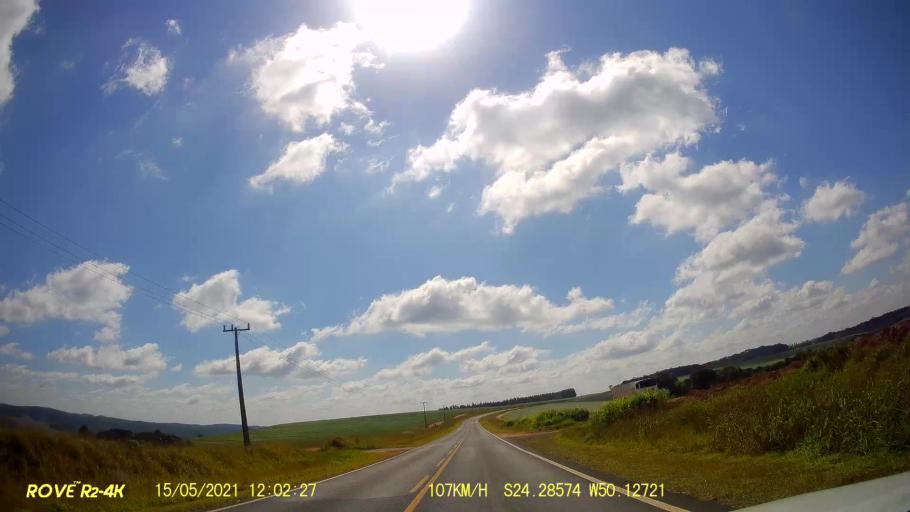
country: BR
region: Parana
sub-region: Pirai Do Sul
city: Pirai do Sul
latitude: -24.2860
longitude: -50.1272
